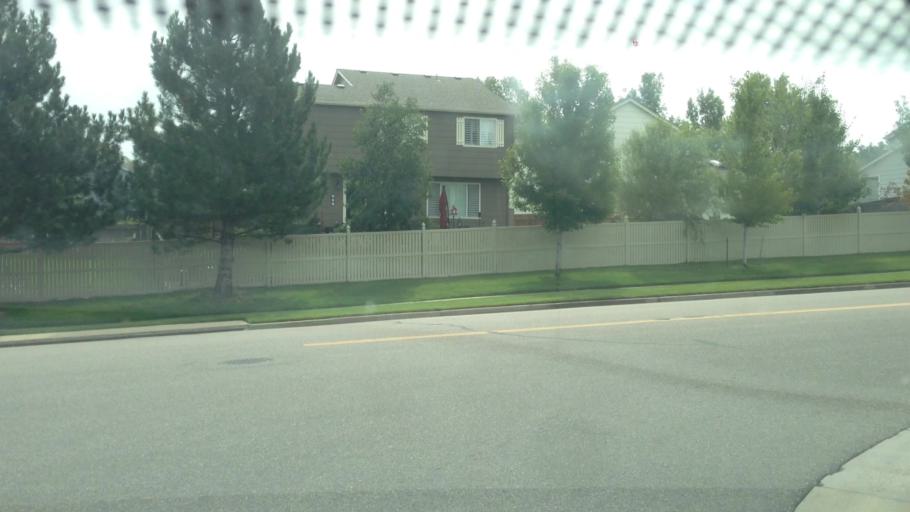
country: US
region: Colorado
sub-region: Douglas County
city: Parker
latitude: 39.6092
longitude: -104.7306
